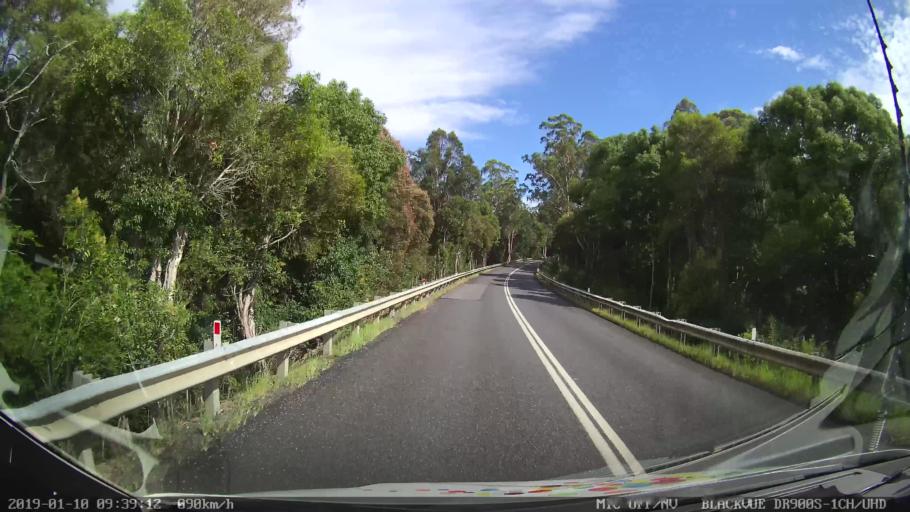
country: AU
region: New South Wales
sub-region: Coffs Harbour
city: Nana Glen
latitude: -30.1662
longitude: 153.0029
